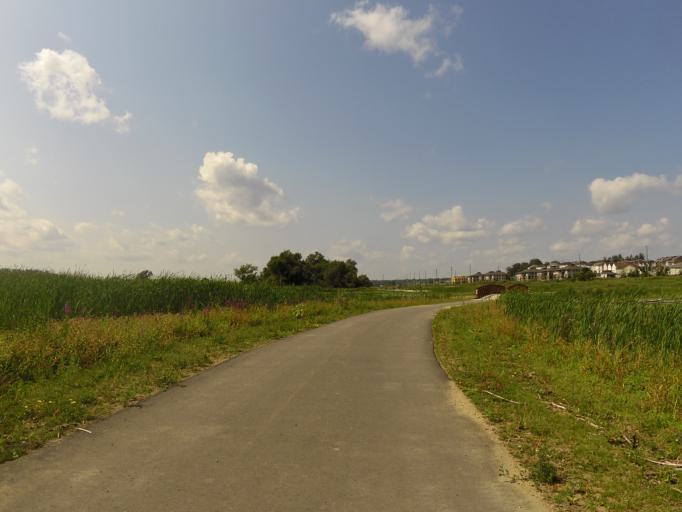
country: CA
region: Ontario
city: Bells Corners
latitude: 45.3095
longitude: -75.9329
